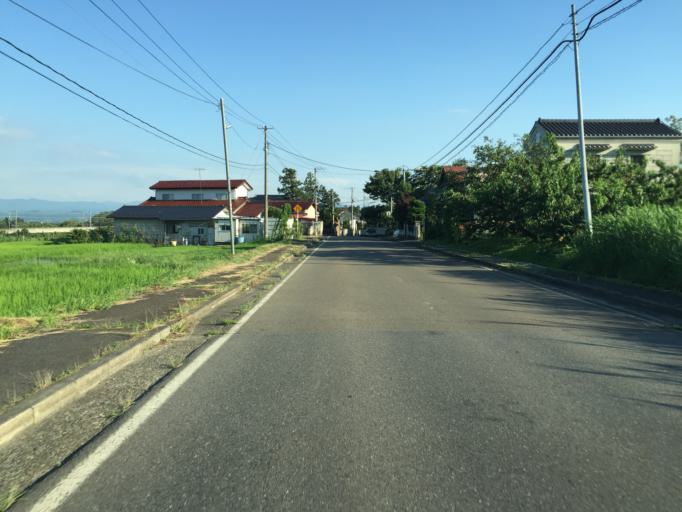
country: JP
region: Fukushima
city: Hobaramachi
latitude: 37.8683
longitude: 140.5225
